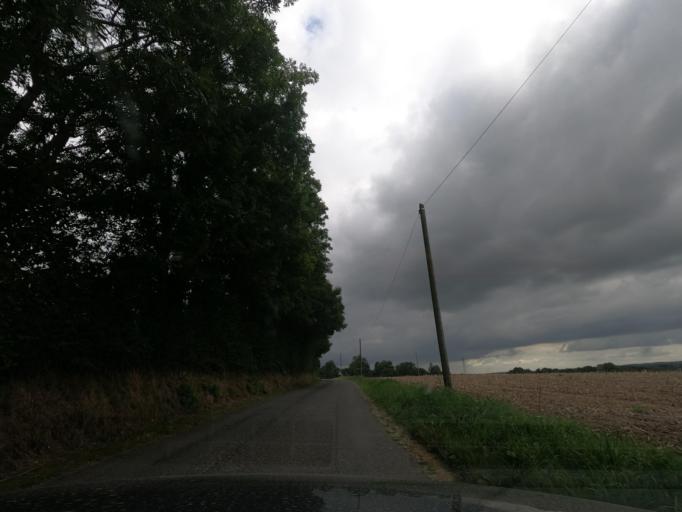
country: FR
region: Lower Normandy
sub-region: Departement de l'Orne
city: Briouze
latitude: 48.7168
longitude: -0.3268
